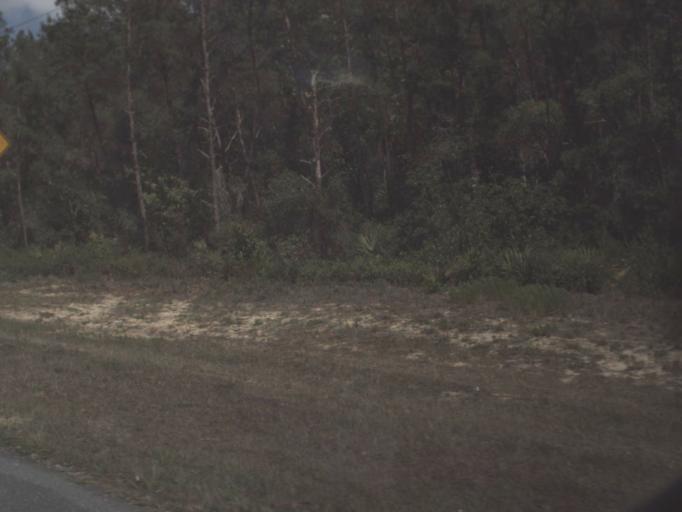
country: US
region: Florida
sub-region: Marion County
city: Silver Springs Shores
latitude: 29.1771
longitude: -81.7881
